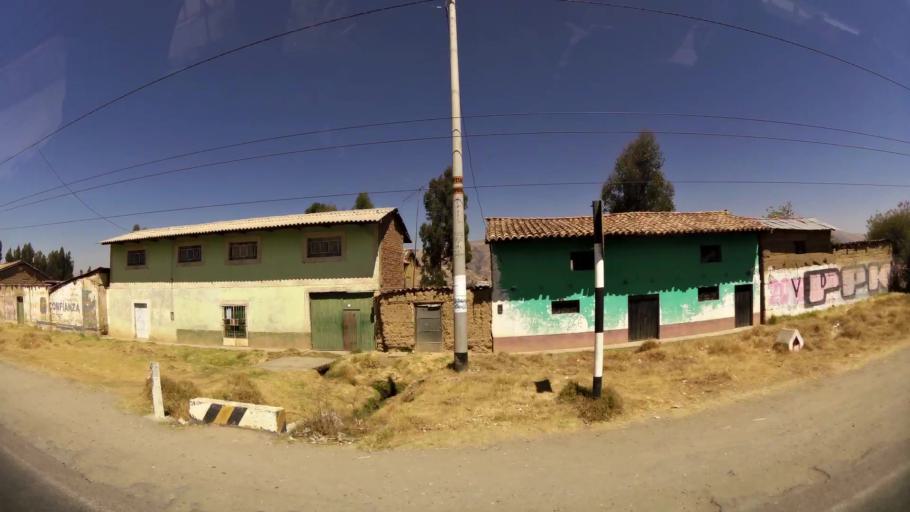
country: PE
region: Junin
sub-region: Provincia de Jauja
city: San Lorenzo
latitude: -11.8494
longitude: -75.3837
